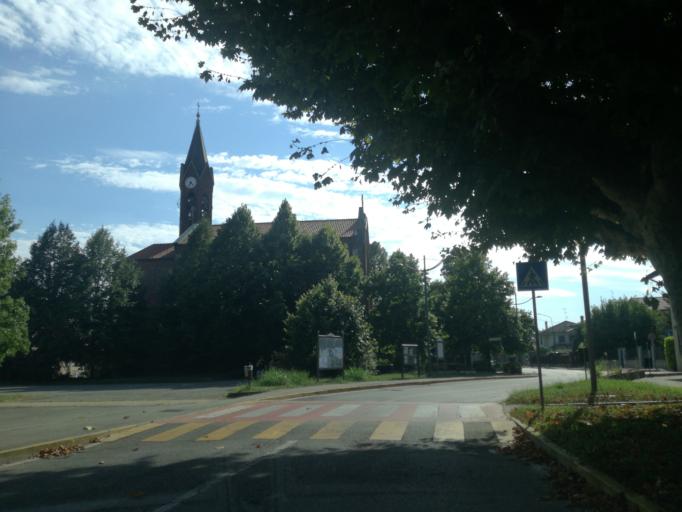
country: IT
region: Lombardy
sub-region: Provincia di Monza e Brianza
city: Velasca
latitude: 45.6349
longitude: 9.3510
